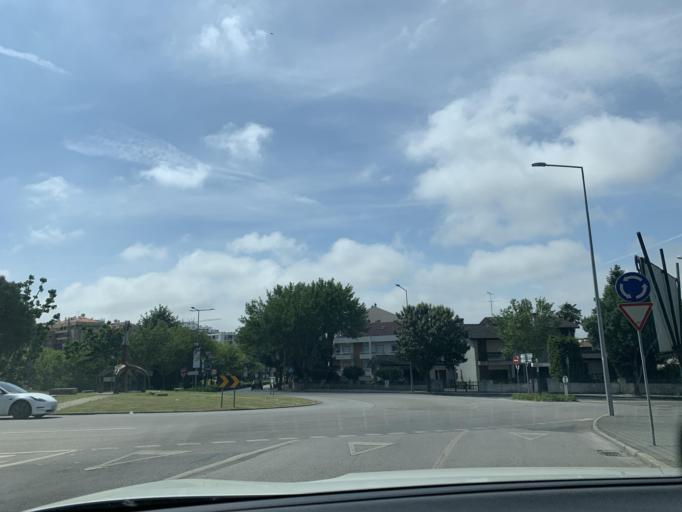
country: PT
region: Viseu
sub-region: Viseu
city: Viseu
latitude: 40.6547
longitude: -7.9224
